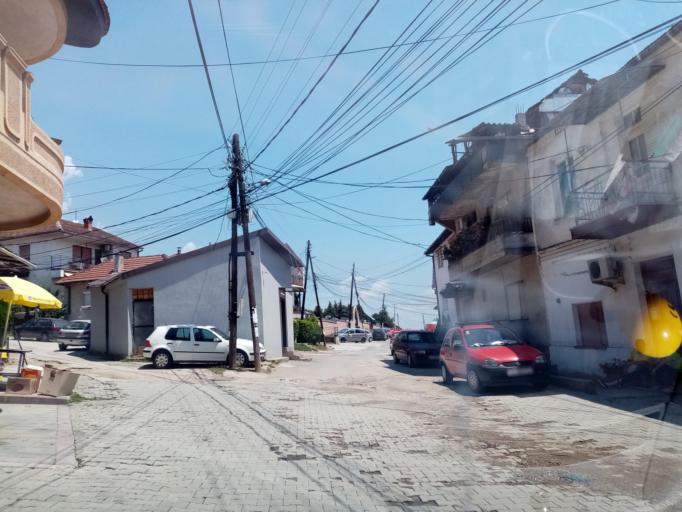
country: MK
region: Tetovo
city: Tetovo
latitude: 42.0166
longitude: 20.9713
